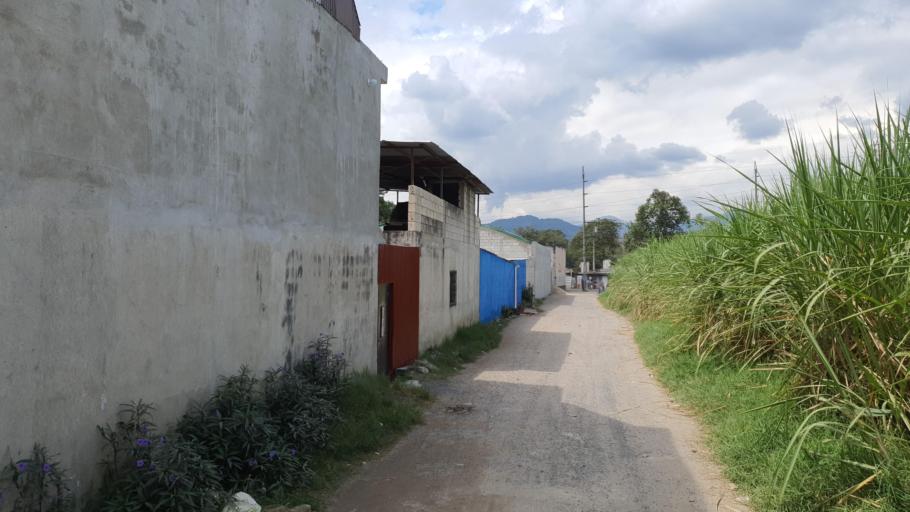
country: GT
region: Guatemala
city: Villa Canales
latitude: 14.4577
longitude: -90.5575
